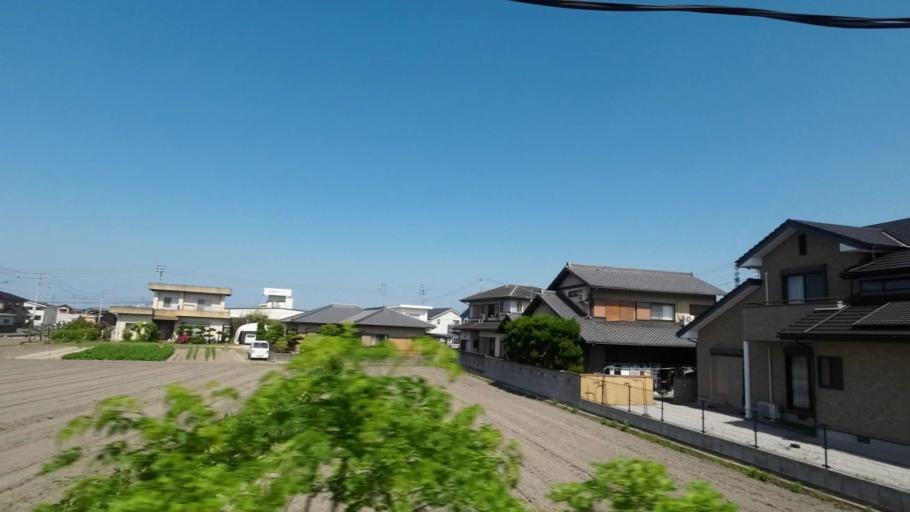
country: JP
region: Kagawa
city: Kan'onjicho
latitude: 34.1214
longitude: 133.6484
